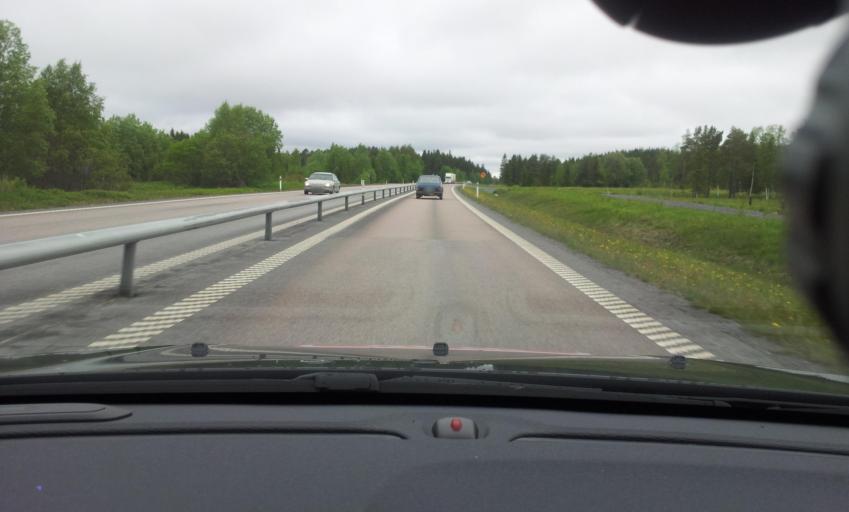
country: SE
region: Jaemtland
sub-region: OEstersunds Kommun
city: Ostersund
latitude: 63.2599
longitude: 14.5512
